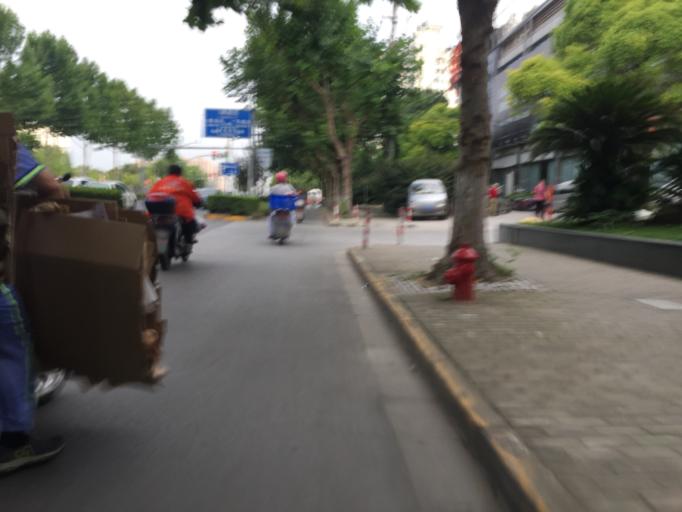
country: CN
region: Shanghai Shi
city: Huamu
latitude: 31.1829
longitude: 121.5373
